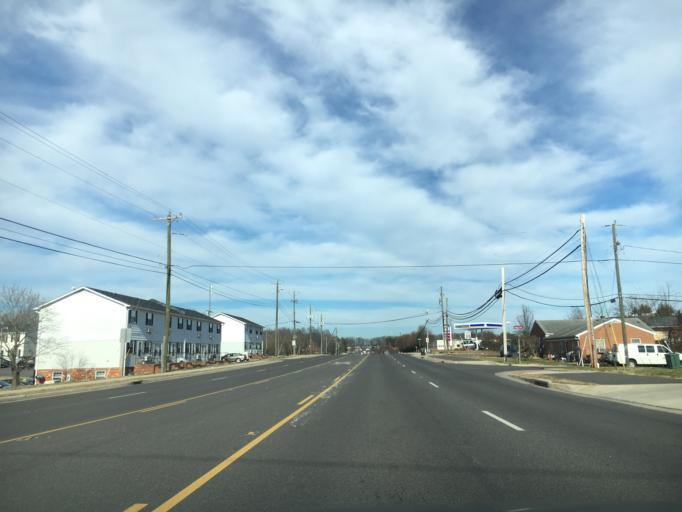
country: US
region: Virginia
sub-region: Culpeper County
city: Culpeper
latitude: 38.4898
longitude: -77.9935
